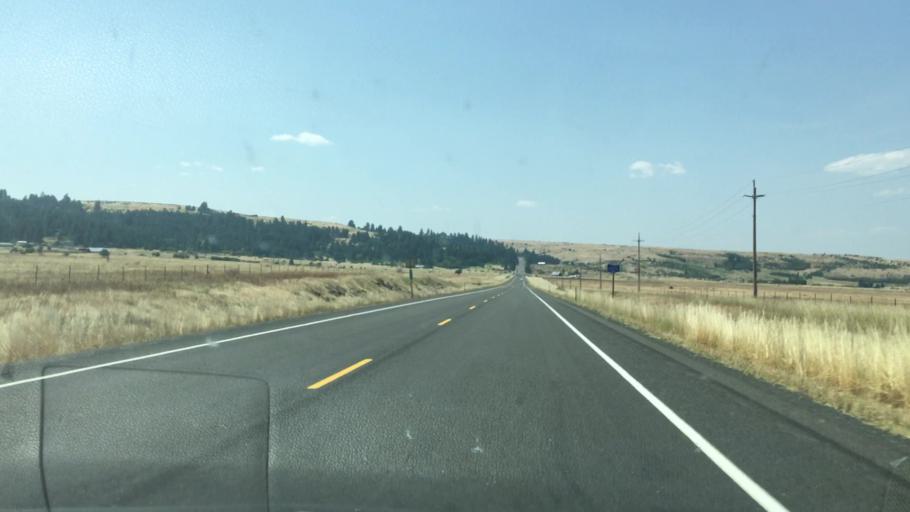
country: US
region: Idaho
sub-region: Idaho County
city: Grangeville
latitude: 45.8870
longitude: -116.2031
